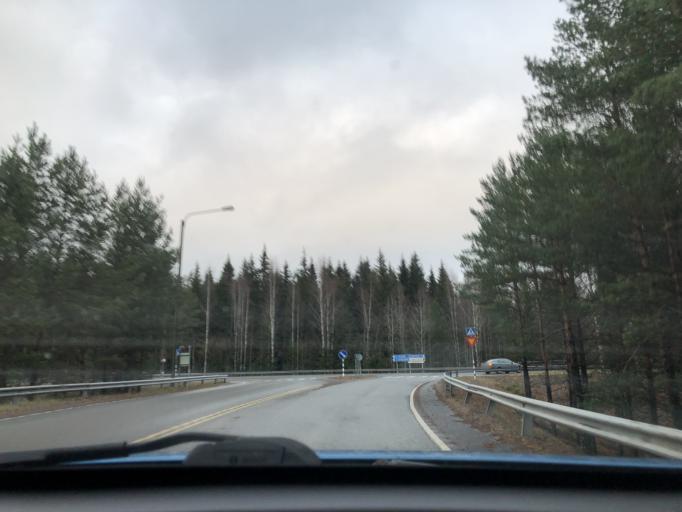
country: FI
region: Pirkanmaa
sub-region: Tampere
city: Kangasala
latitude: 61.5329
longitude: 23.9492
